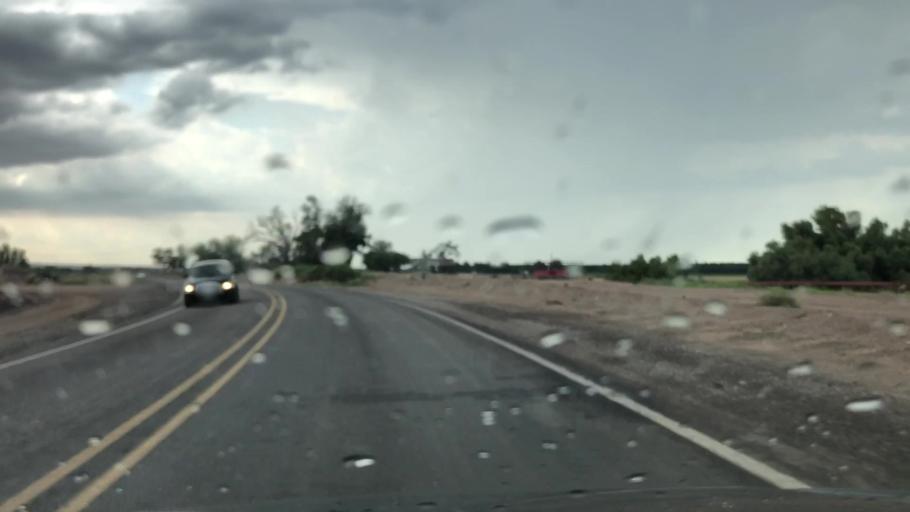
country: US
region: New Mexico
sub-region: Dona Ana County
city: Vado
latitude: 32.0681
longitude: -106.6799
